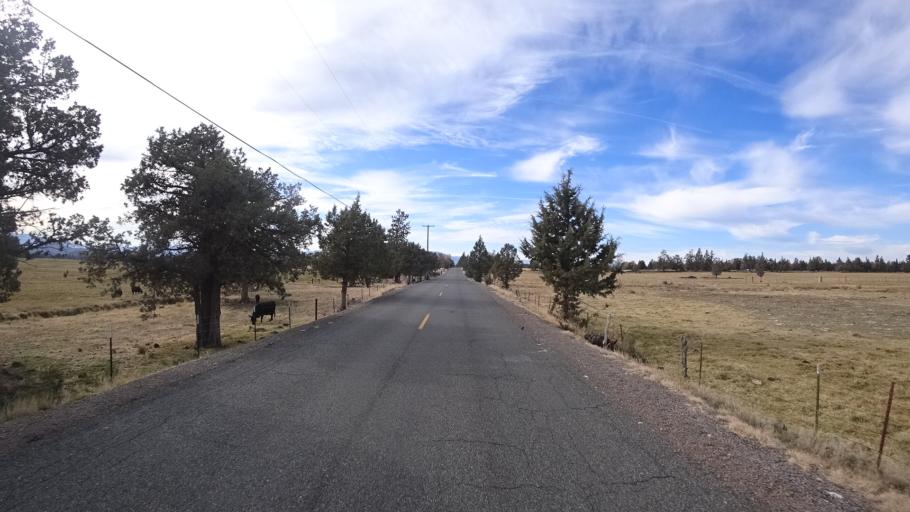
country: US
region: California
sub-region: Siskiyou County
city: Montague
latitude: 41.6384
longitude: -122.4129
